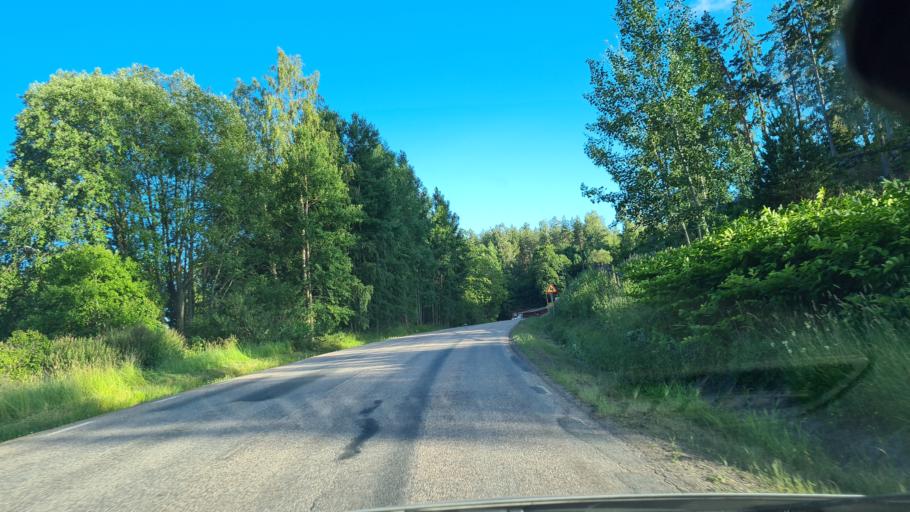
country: SE
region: Soedermanland
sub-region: Gnesta Kommun
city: Gnesta
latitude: 59.0297
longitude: 17.3356
